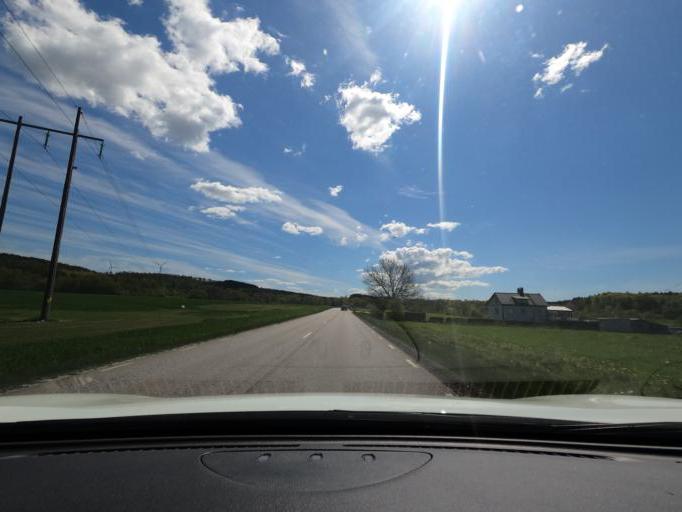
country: SE
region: Halland
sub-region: Kungsbacka Kommun
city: Fjaeras kyrkby
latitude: 57.4215
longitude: 12.2011
